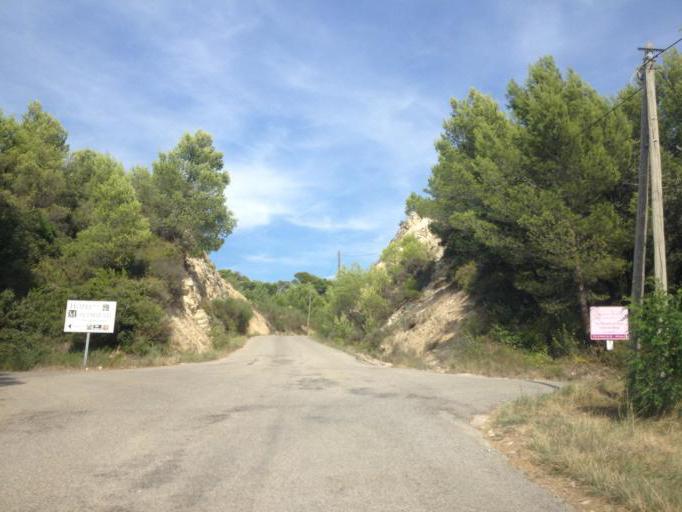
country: FR
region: Provence-Alpes-Cote d'Azur
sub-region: Departement du Vaucluse
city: Vacqueyras
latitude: 44.1360
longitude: 5.0052
